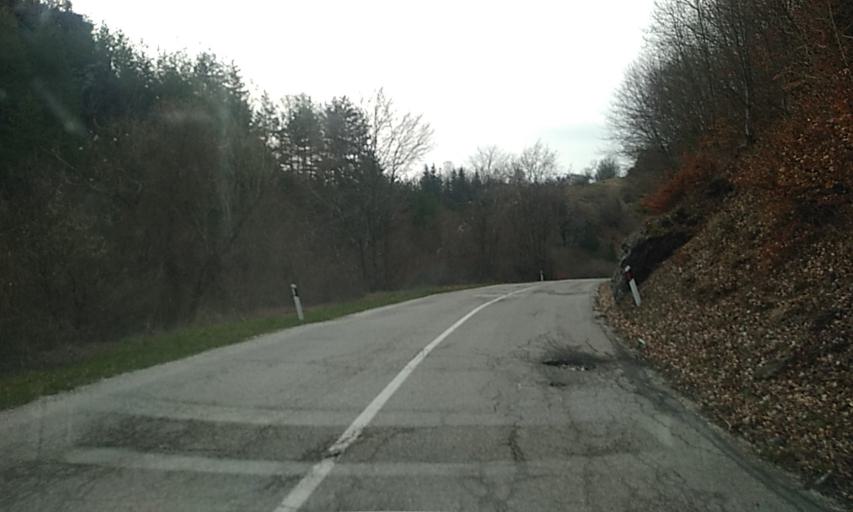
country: RS
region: Central Serbia
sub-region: Pcinjski Okrug
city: Bosilegrad
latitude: 42.5423
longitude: 22.4040
